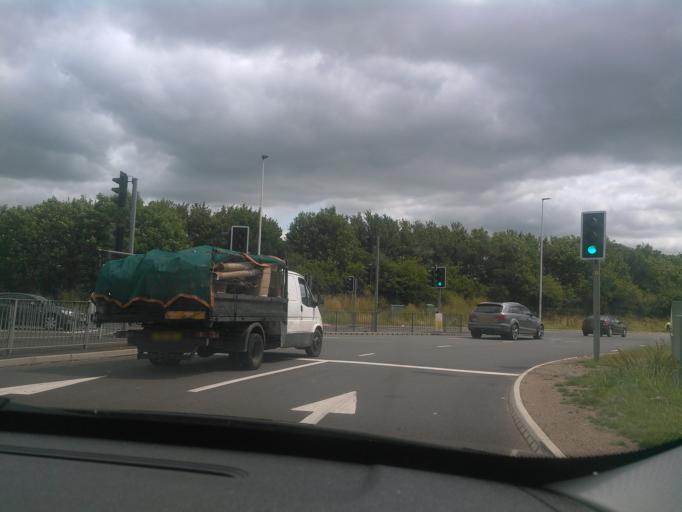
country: GB
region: England
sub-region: Shropshire
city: Berrington
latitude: 52.6924
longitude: -2.7104
